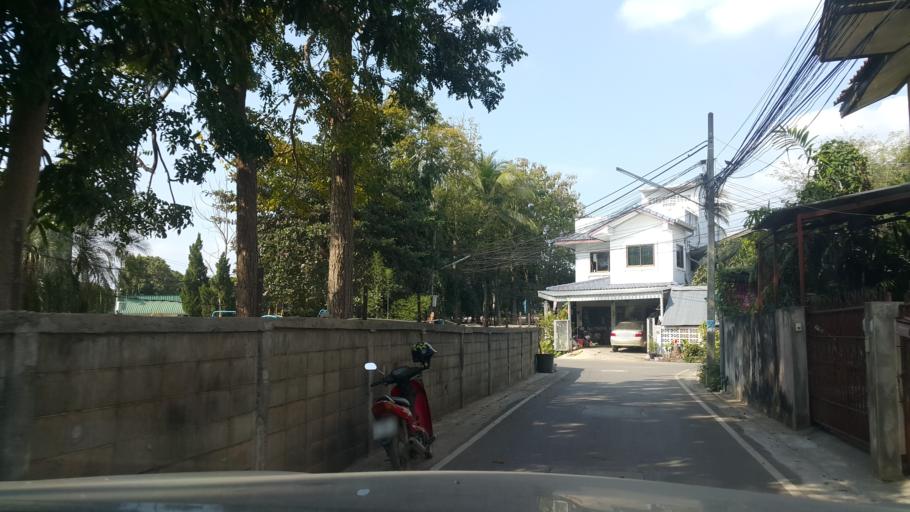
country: TH
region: Phayao
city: Phayao
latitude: 19.1679
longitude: 99.8971
